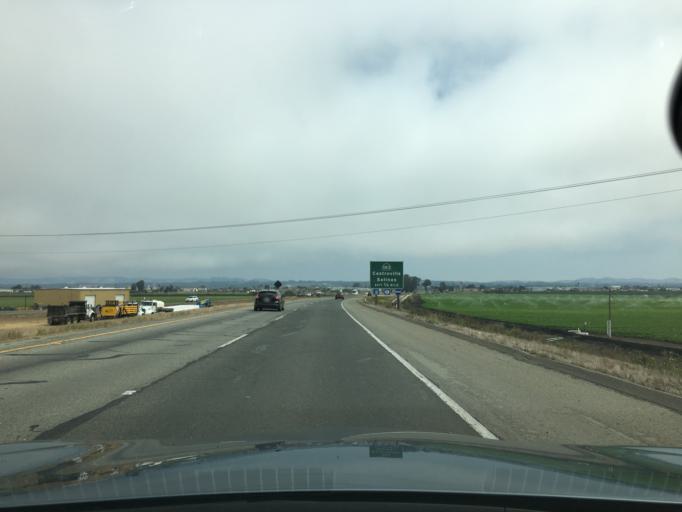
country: US
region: California
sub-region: Monterey County
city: Castroville
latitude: 36.7529
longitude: -121.7645
